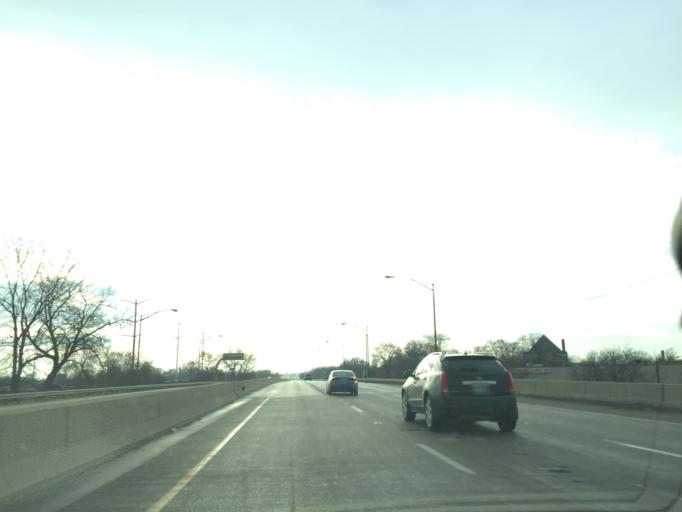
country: US
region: Illinois
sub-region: Cook County
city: Chicago
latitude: 41.7642
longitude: -87.6060
